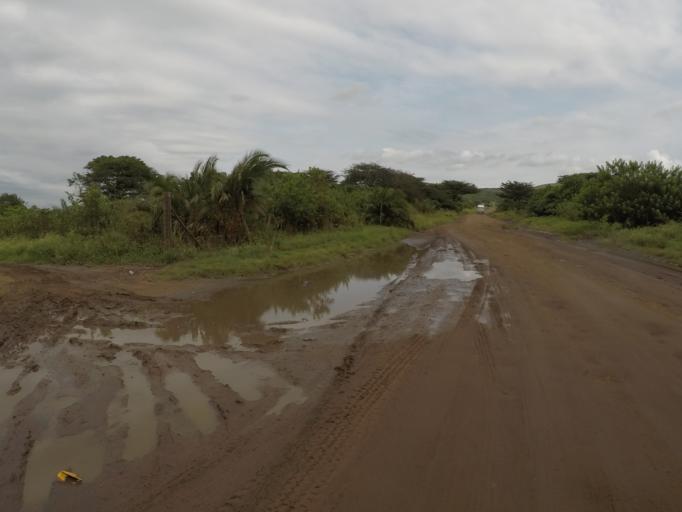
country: ZA
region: KwaZulu-Natal
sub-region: uThungulu District Municipality
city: Empangeni
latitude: -28.7148
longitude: 31.8652
